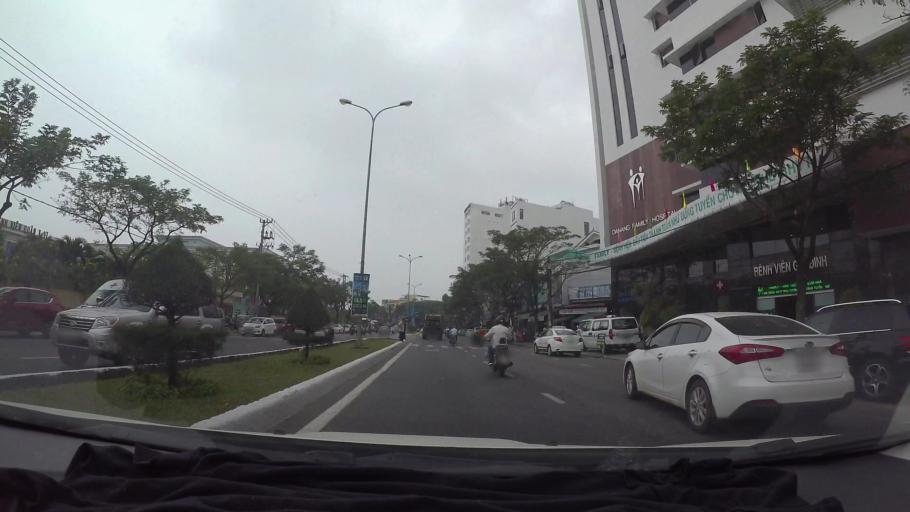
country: VN
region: Da Nang
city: Da Nang
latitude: 16.0537
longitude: 108.2088
